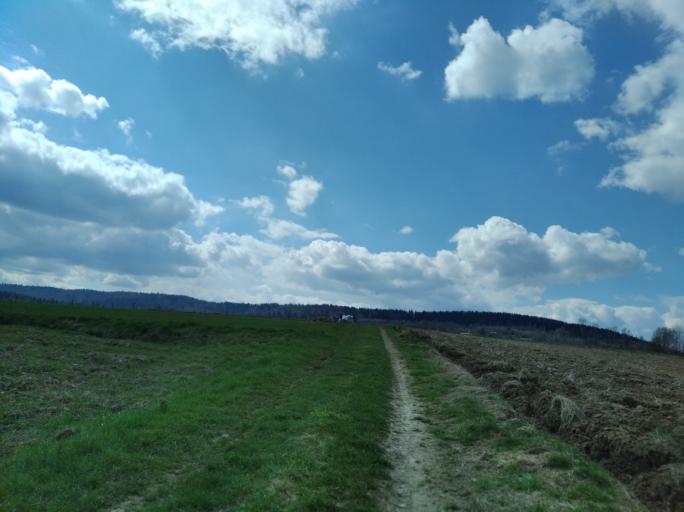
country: PL
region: Subcarpathian Voivodeship
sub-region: Powiat strzyzowski
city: Strzyzow
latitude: 49.8440
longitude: 21.7805
